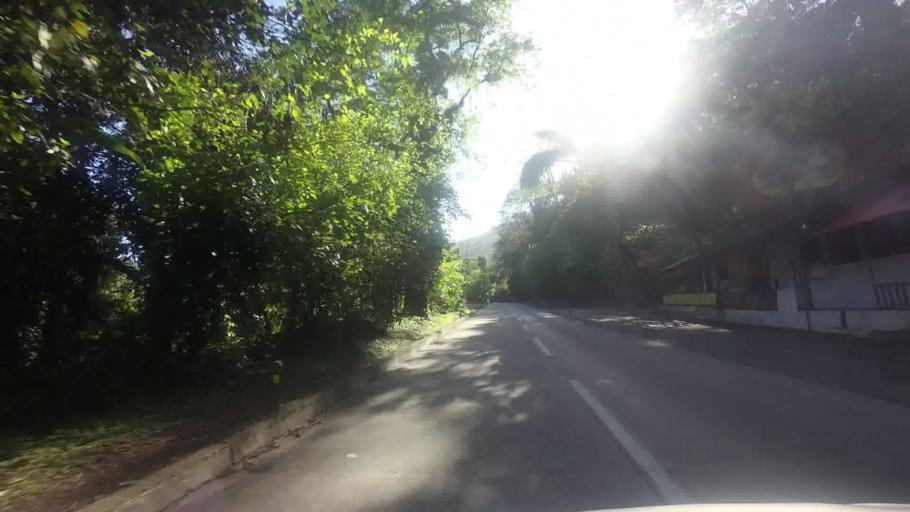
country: BR
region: Rio de Janeiro
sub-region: Petropolis
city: Petropolis
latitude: -22.5874
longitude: -43.2669
